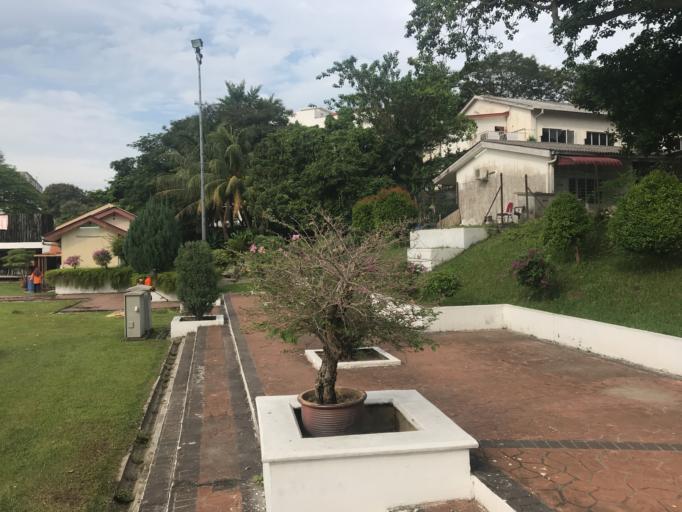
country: MY
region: Perak
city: Ipoh
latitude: 4.5992
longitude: 101.0758
